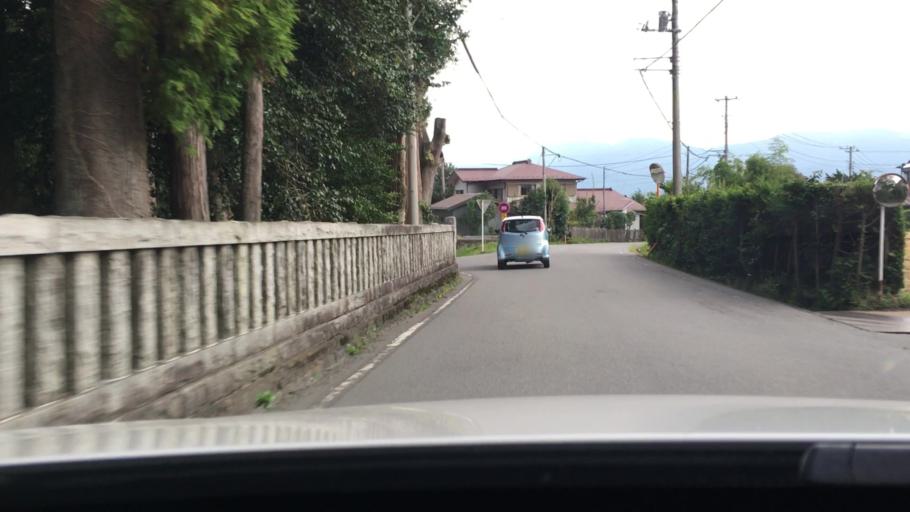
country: JP
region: Shizuoka
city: Gotemba
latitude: 35.3213
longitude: 138.9039
